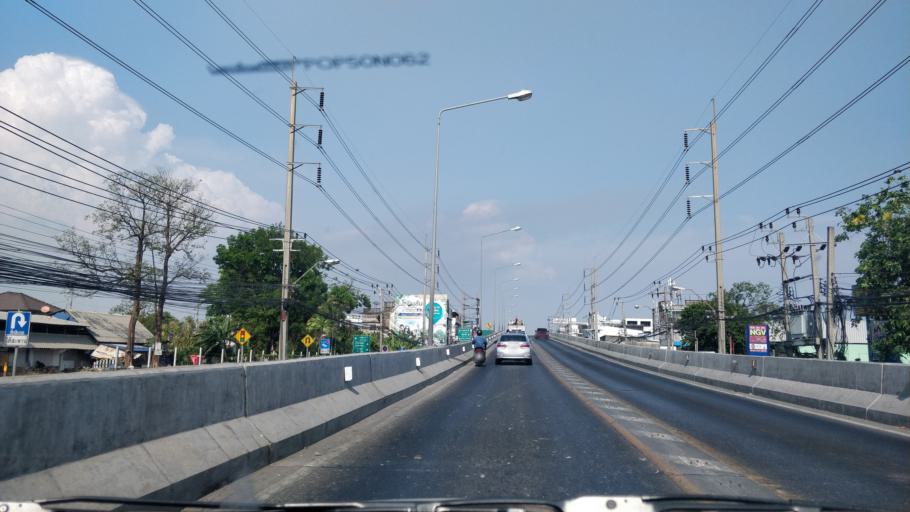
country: TH
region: Bangkok
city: Suan Luang
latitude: 13.7213
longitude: 100.6958
